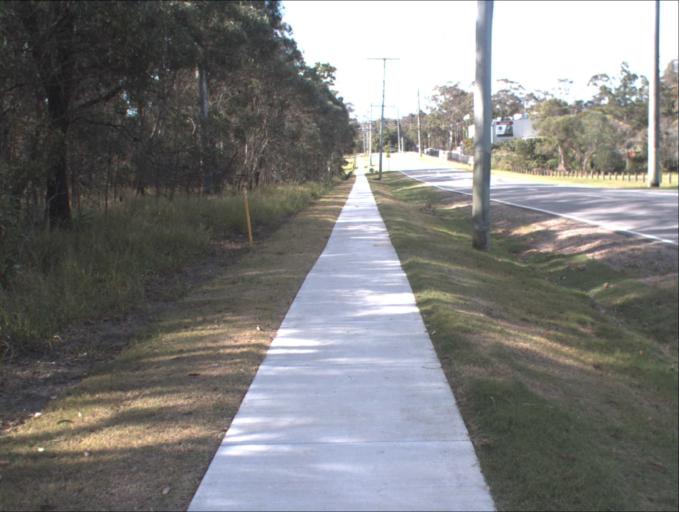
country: AU
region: Queensland
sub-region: Logan
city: Slacks Creek
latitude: -27.6480
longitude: 153.1358
